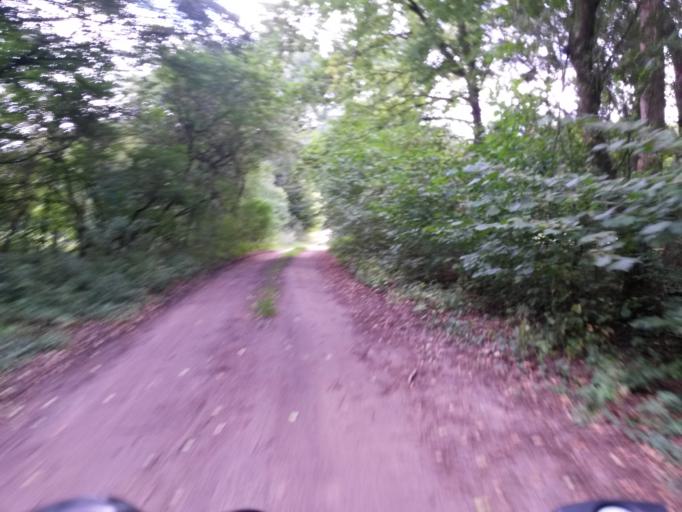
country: DE
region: Brandenburg
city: Templin
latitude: 53.0884
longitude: 13.5408
